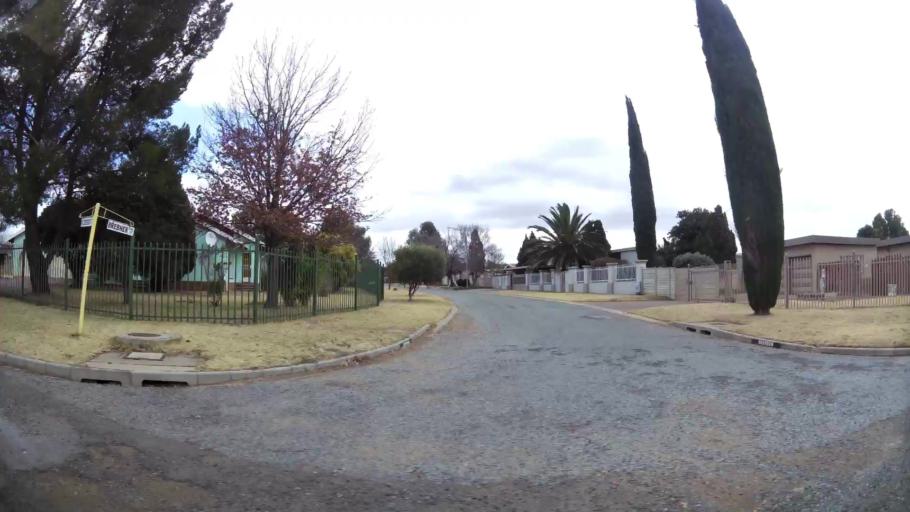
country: ZA
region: Orange Free State
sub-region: Fezile Dabi District Municipality
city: Kroonstad
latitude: -27.6340
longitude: 27.2444
